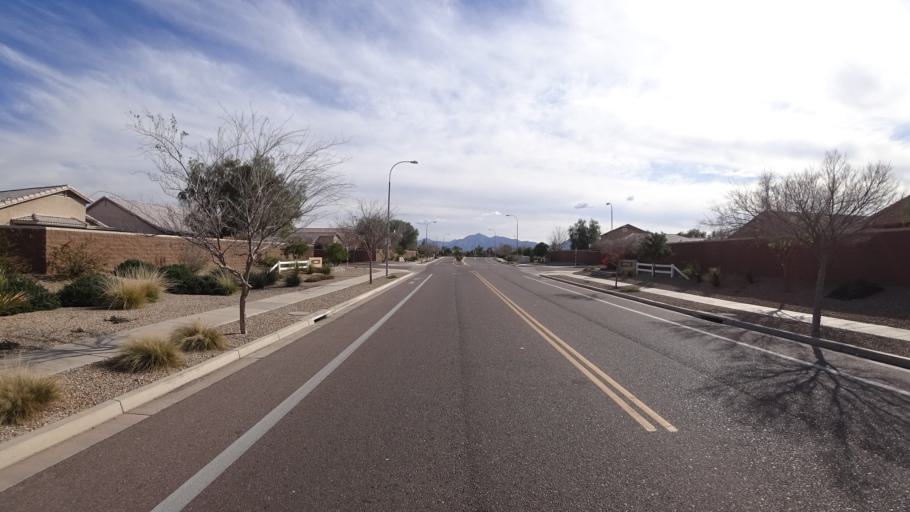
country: US
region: Arizona
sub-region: Maricopa County
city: Tolleson
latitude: 33.4225
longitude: -112.2810
